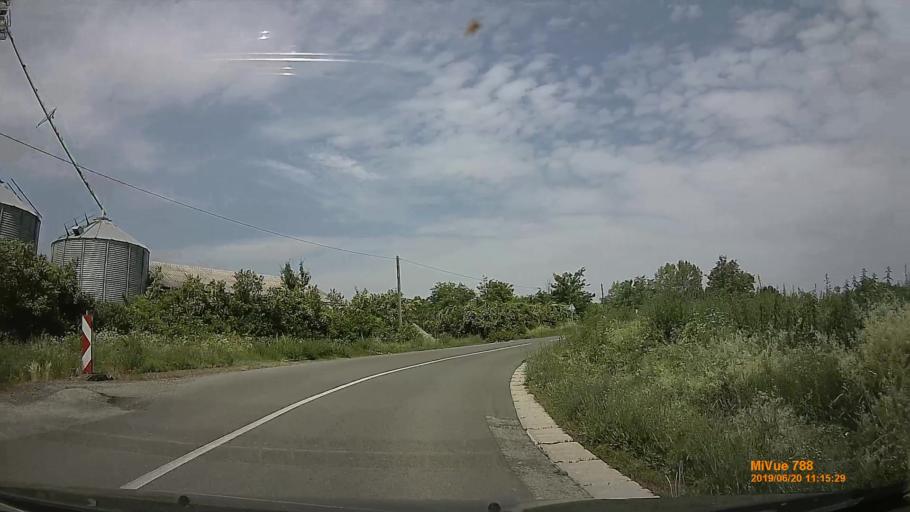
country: HU
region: Baranya
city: Pecsvarad
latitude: 46.1506
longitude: 18.4871
